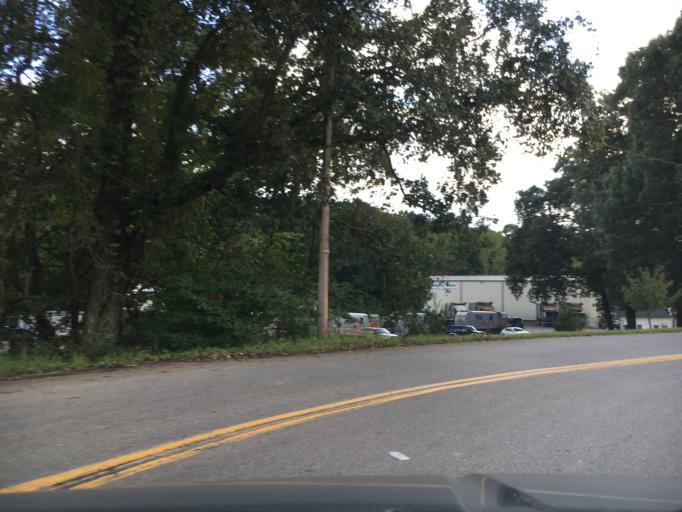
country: US
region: Virginia
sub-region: City of Lynchburg
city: Lynchburg
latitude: 37.3792
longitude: -79.1438
